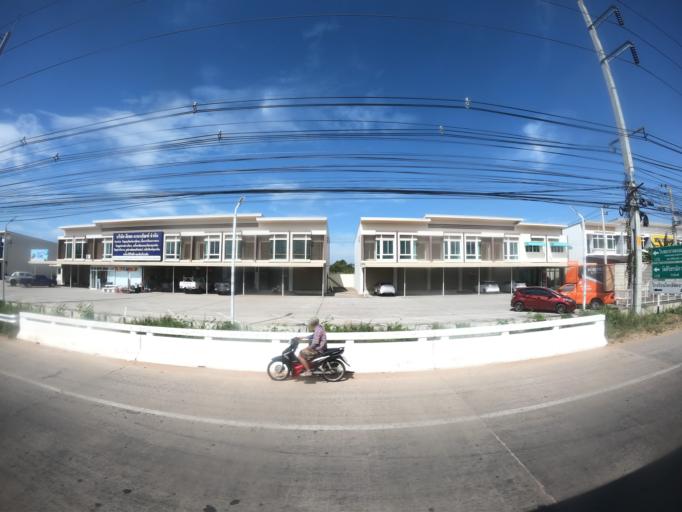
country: TH
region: Khon Kaen
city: Khon Kaen
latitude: 16.4450
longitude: 102.9473
